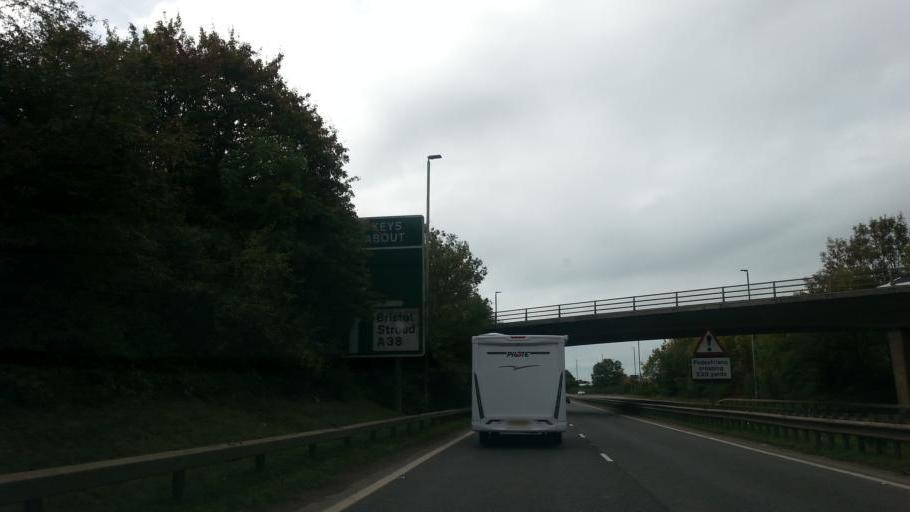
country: GB
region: England
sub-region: Gloucestershire
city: Stonehouse
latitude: 51.8112
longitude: -2.2839
